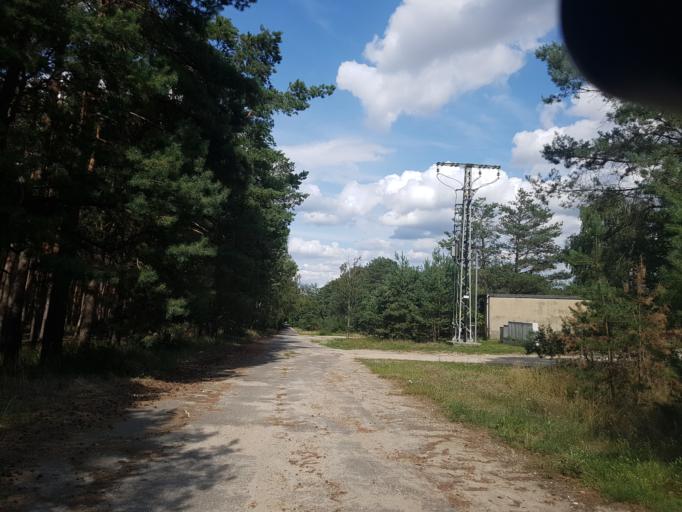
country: DE
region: Brandenburg
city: Schonborn
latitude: 51.6587
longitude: 13.4991
